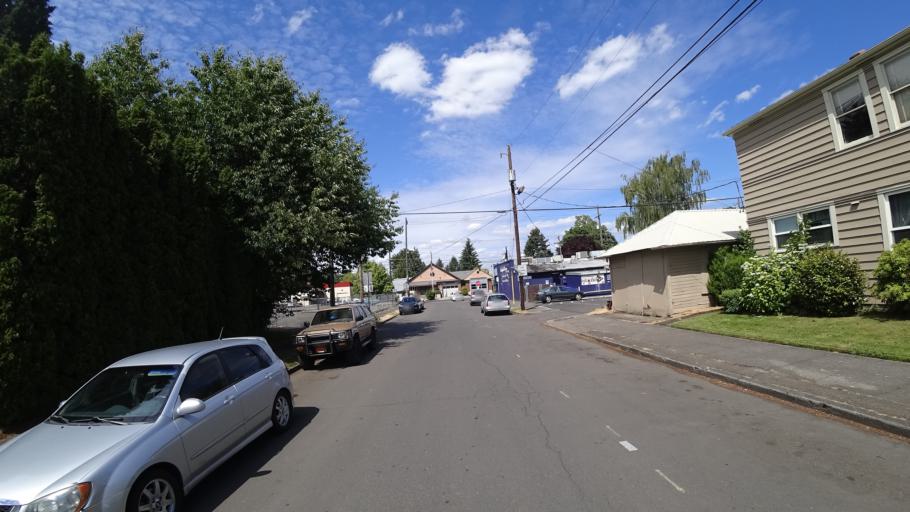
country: US
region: Oregon
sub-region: Multnomah County
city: Portland
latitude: 45.5815
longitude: -122.7232
